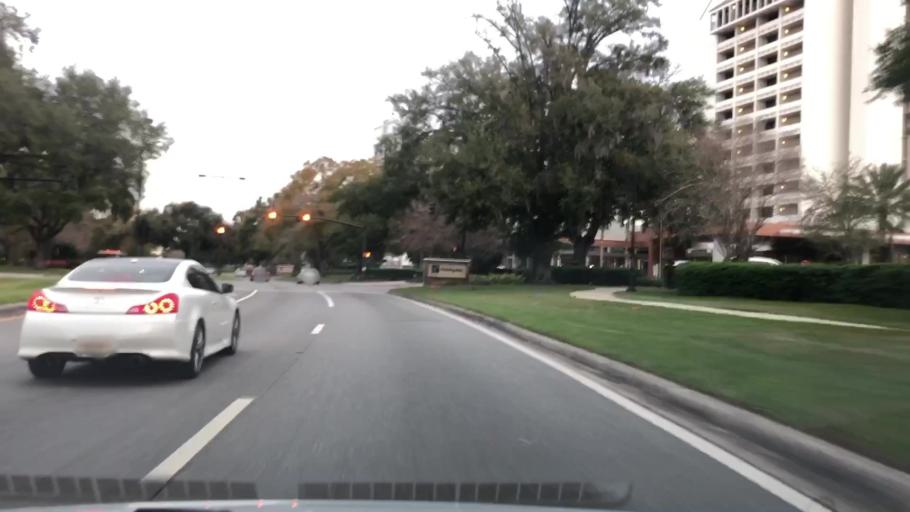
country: US
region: Florida
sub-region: Osceola County
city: Celebration
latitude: 28.3751
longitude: -81.5094
